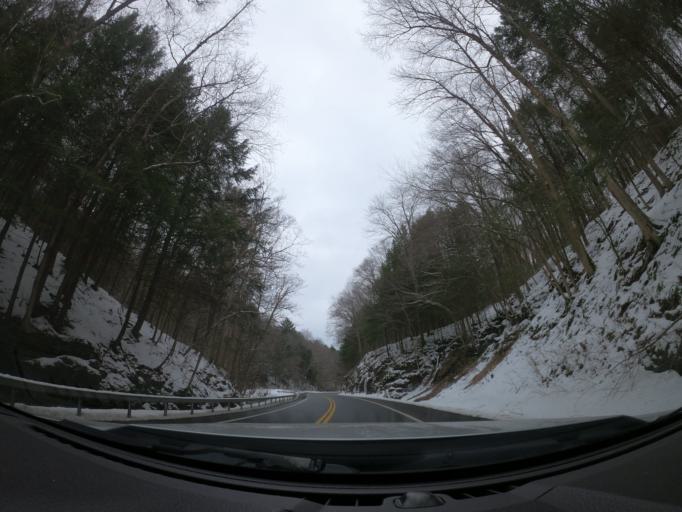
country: US
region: New York
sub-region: Cortland County
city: Homer
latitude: 42.6671
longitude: -76.2342
